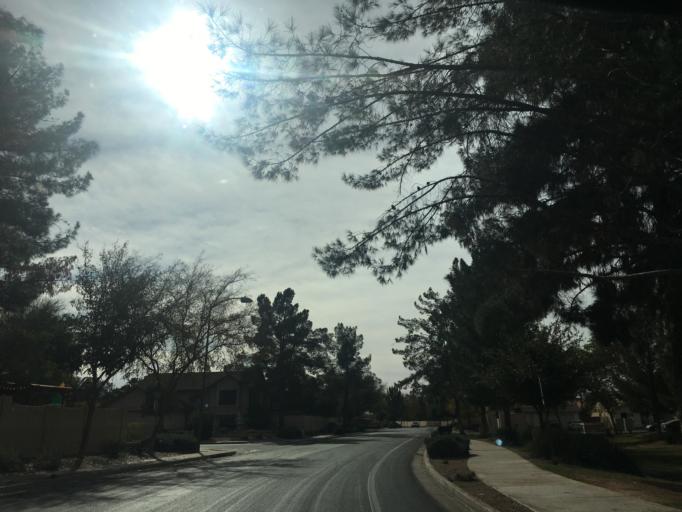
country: US
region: Arizona
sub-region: Maricopa County
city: Gilbert
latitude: 33.3456
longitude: -111.8032
